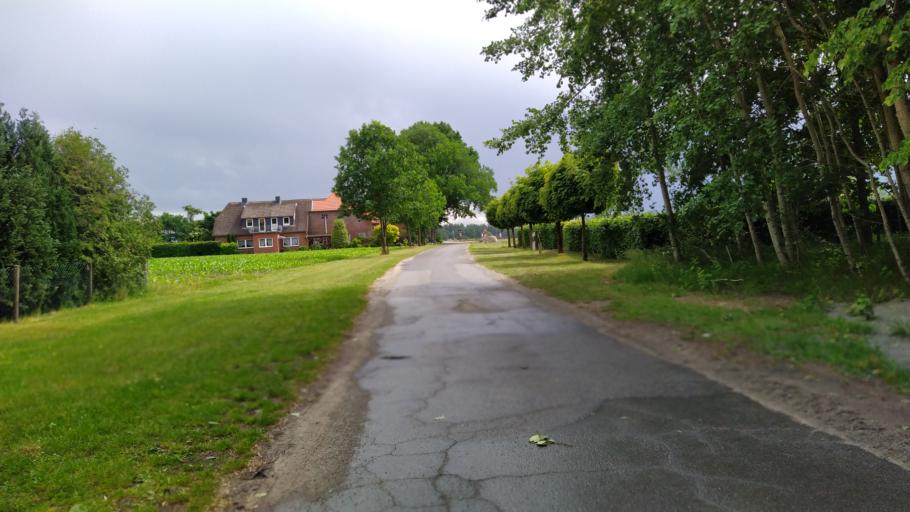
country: DE
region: Lower Saxony
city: Kutenholz
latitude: 53.4677
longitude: 9.3438
